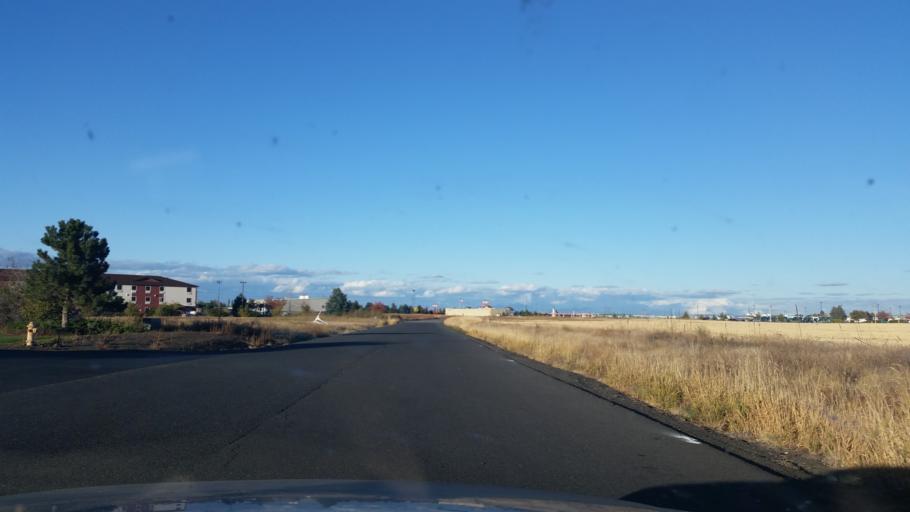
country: US
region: Washington
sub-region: Spokane County
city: Airway Heights
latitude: 47.5847
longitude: -117.5696
